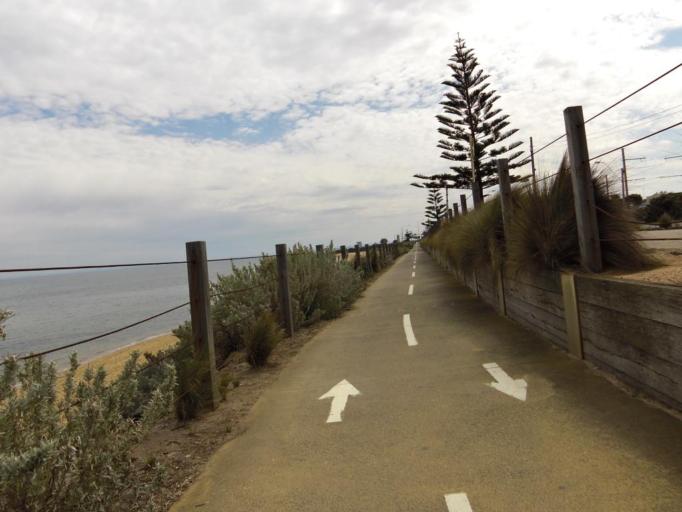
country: AU
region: Victoria
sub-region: Bayside
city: Hampton
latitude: -37.9293
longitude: 144.9902
